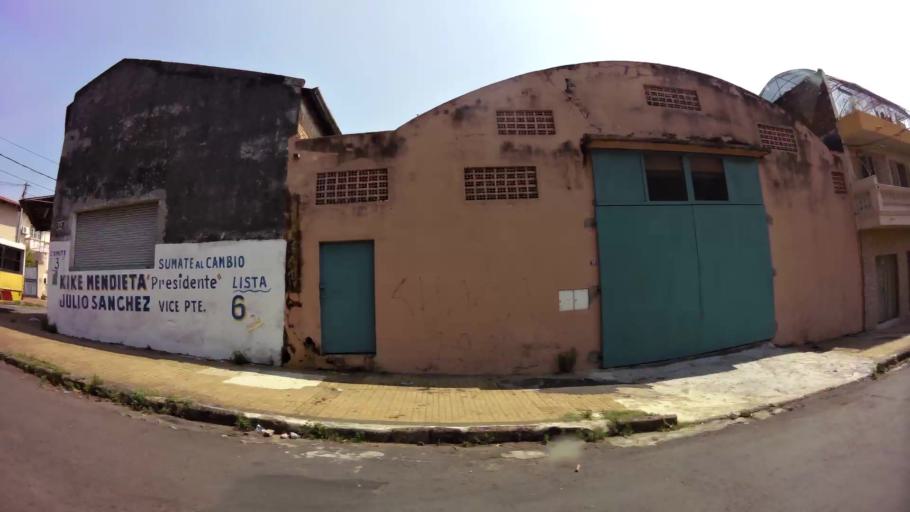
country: PY
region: Asuncion
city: Asuncion
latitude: -25.2838
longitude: -57.6498
